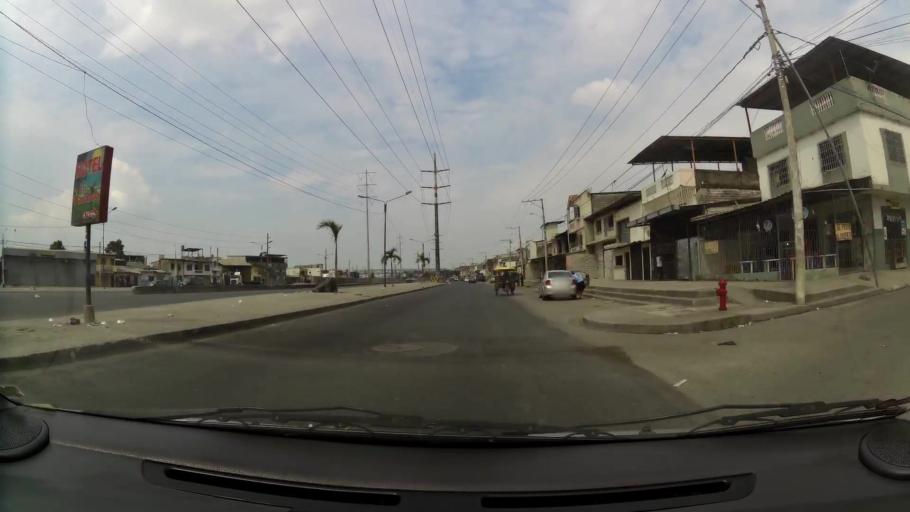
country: EC
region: Guayas
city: Guayaquil
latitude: -2.2396
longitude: -79.9232
